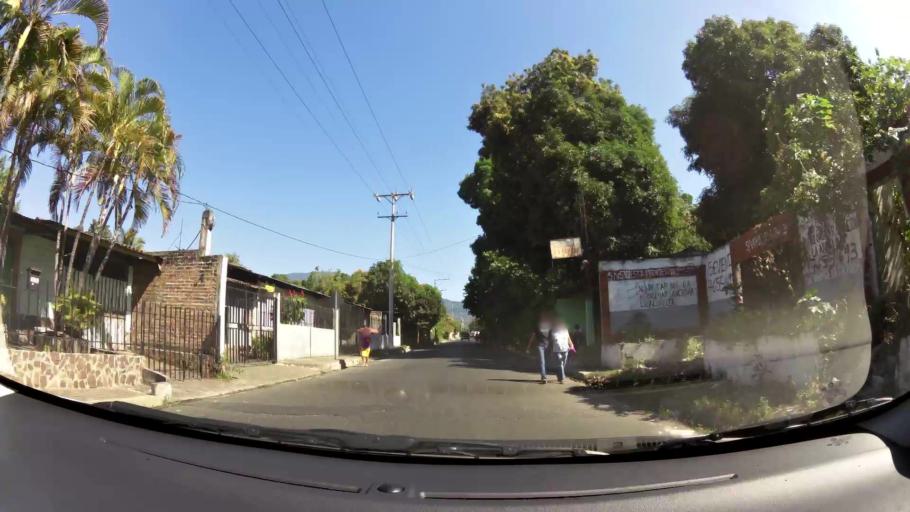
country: SV
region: La Libertad
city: Santa Tecla
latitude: 13.7320
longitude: -89.3731
